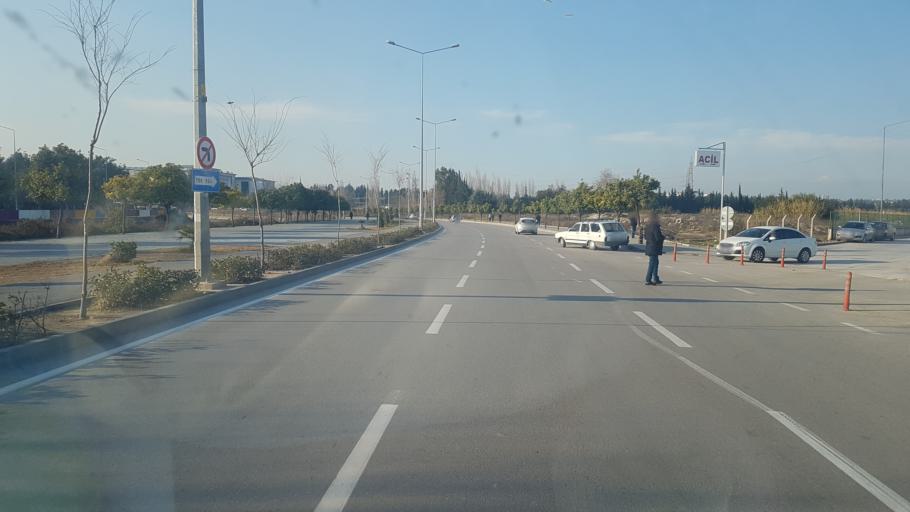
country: TR
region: Adana
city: Adana
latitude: 37.0102
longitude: 35.3529
